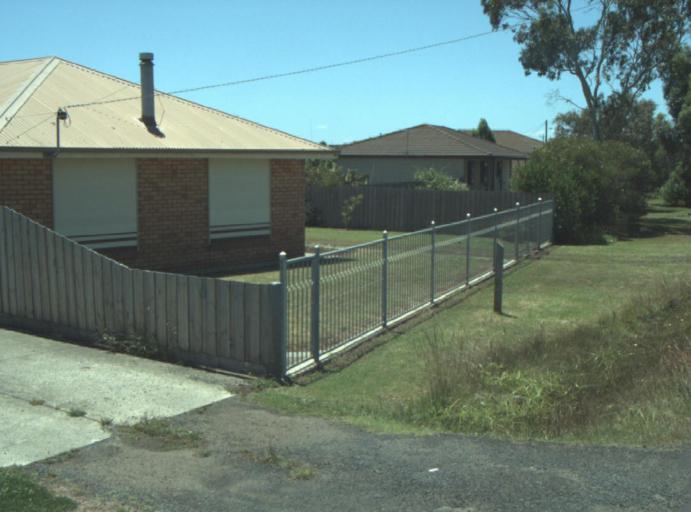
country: AU
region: Victoria
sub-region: Queenscliffe
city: Queenscliff
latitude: -38.1748
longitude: 144.7076
